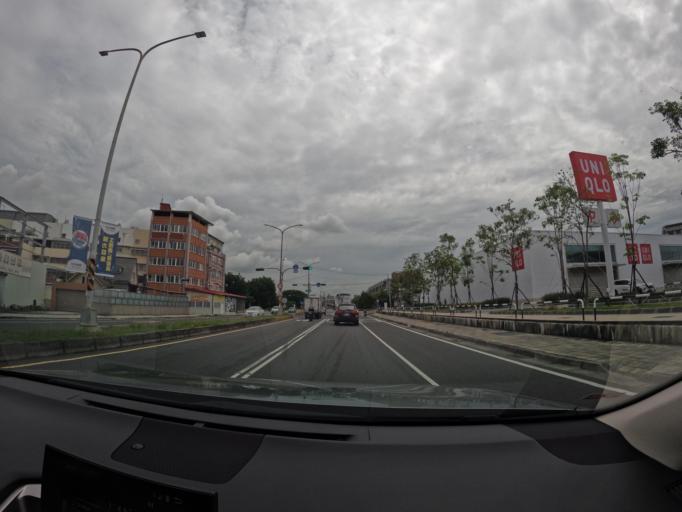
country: TW
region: Kaohsiung
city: Kaohsiung
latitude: 22.7816
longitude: 120.2992
